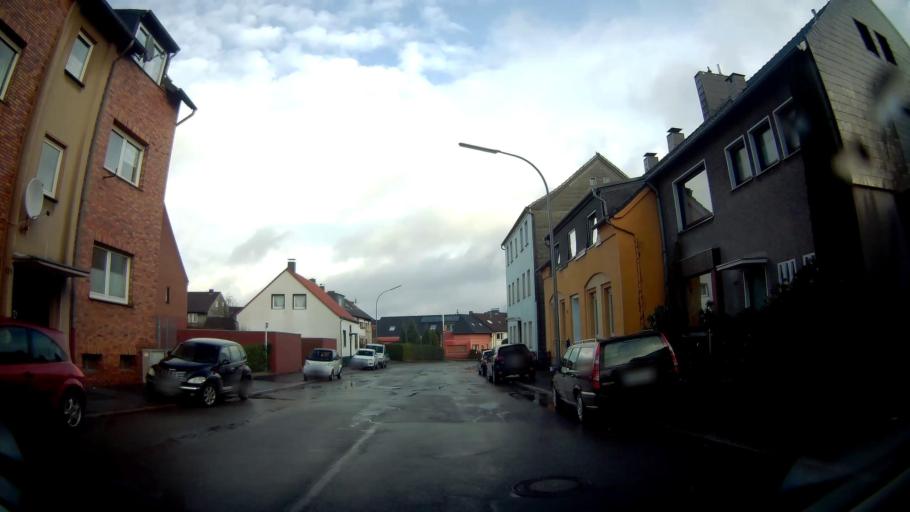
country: DE
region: North Rhine-Westphalia
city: Castrop-Rauxel
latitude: 51.5050
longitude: 7.3156
